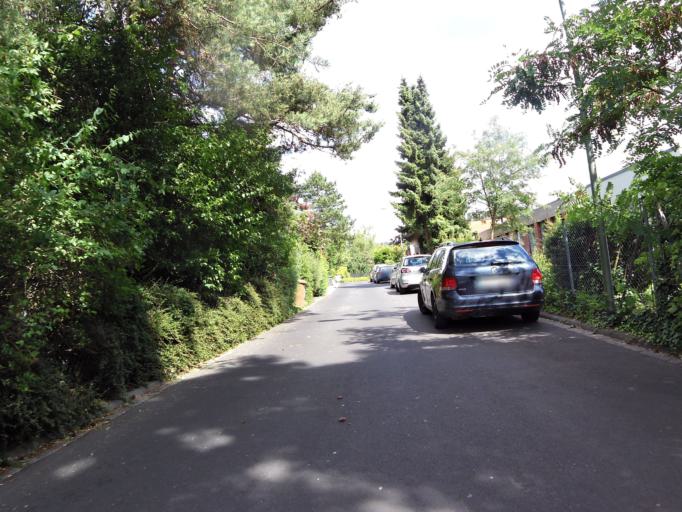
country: DE
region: Bavaria
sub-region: Regierungsbezirk Unterfranken
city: Zell am Main
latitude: 49.8153
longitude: 9.8854
